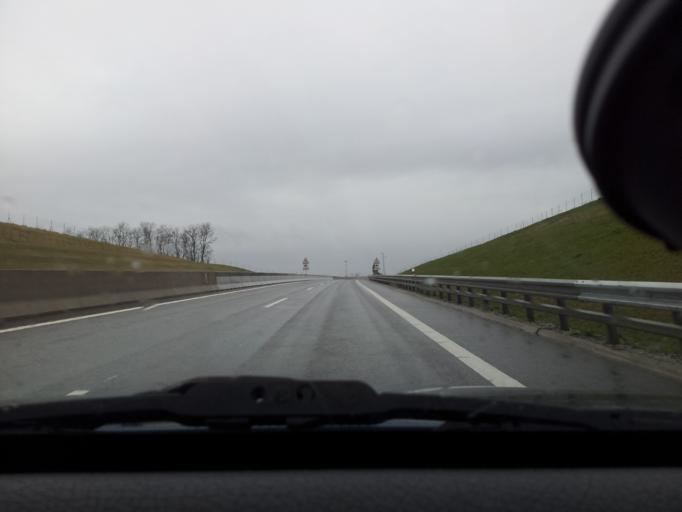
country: SK
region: Nitriansky
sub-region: Okres Nitra
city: Vrable
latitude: 48.3342
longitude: 18.2222
